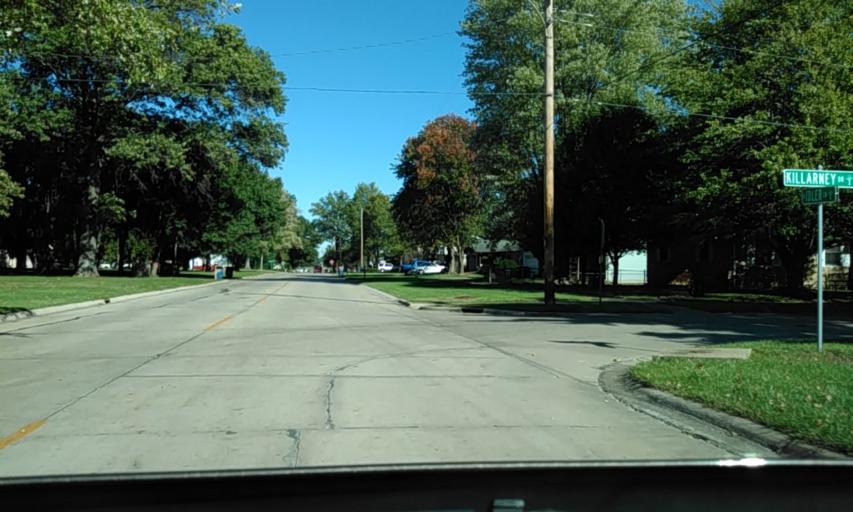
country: US
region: Illinois
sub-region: Bond County
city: Greenville
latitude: 38.8963
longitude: -89.3912
